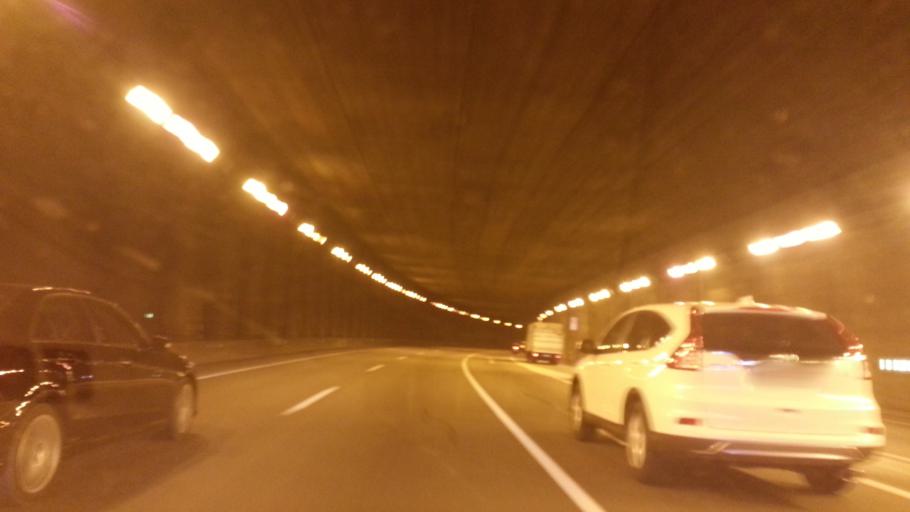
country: ES
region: Catalonia
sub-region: Provincia de Barcelona
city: les Corts
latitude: 41.3986
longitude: 2.1131
